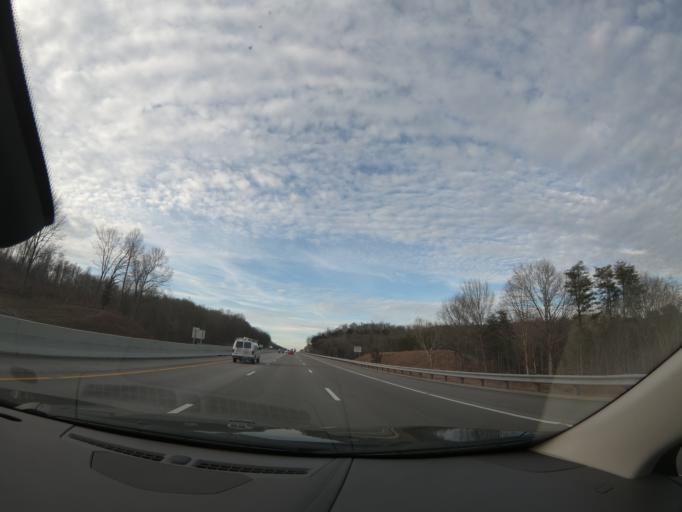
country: US
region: Kentucky
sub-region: Hart County
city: Munfordville
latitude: 37.3014
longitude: -85.9019
